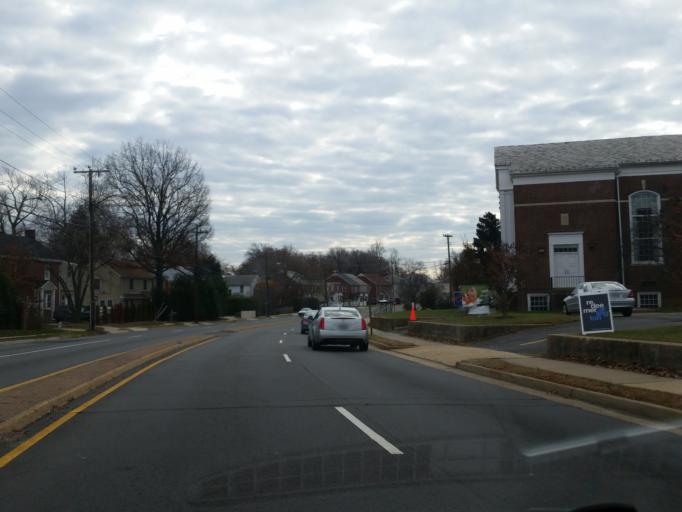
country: US
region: Virginia
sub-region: Arlington County
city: Arlington
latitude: 38.8655
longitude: -77.0931
